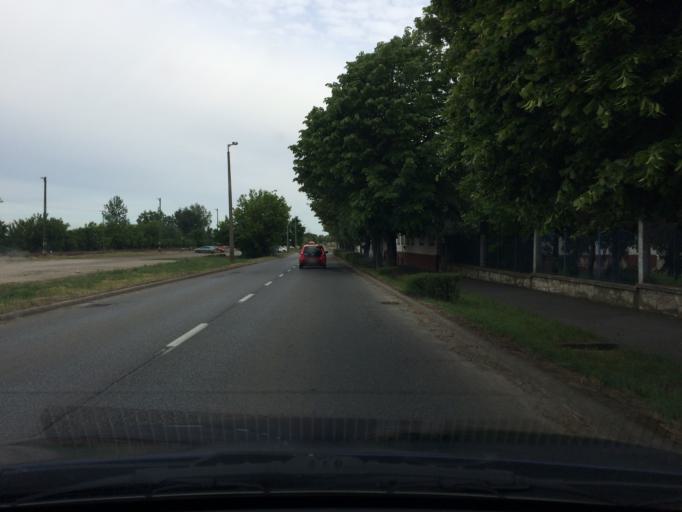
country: HU
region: Szabolcs-Szatmar-Bereg
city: Tiszavasvari
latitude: 47.9449
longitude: 21.3748
